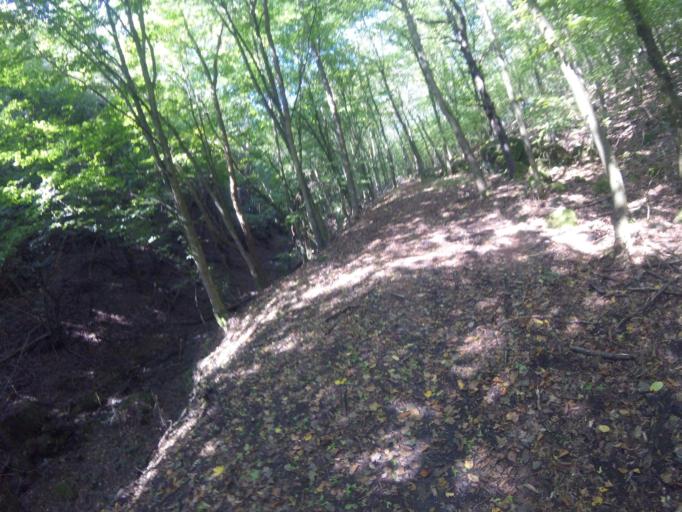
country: HU
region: Nograd
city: Bujak
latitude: 47.8990
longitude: 19.5194
